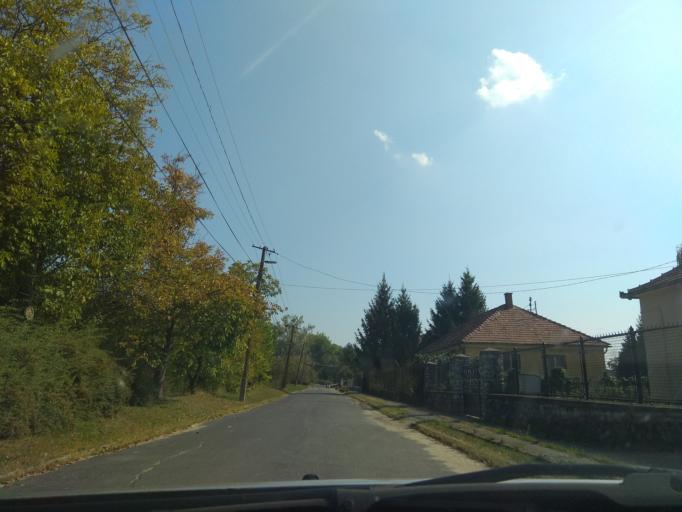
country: HU
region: Borsod-Abauj-Zemplen
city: Miskolc
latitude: 48.0740
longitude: 20.7714
